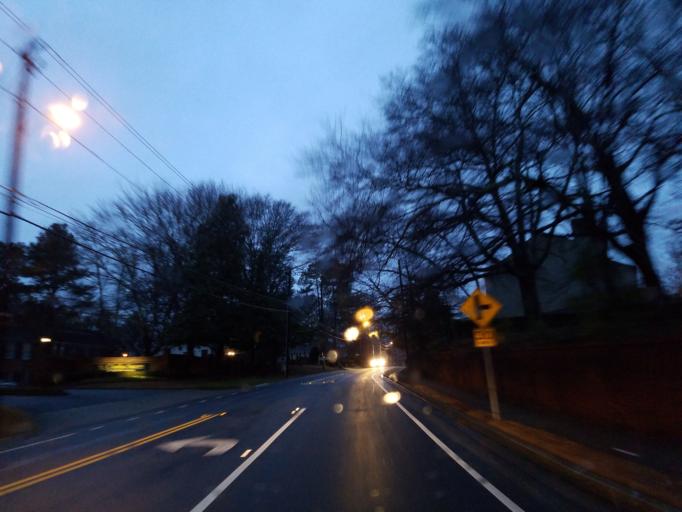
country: US
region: Georgia
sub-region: Fulton County
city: Roswell
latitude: 34.0259
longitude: -84.3530
